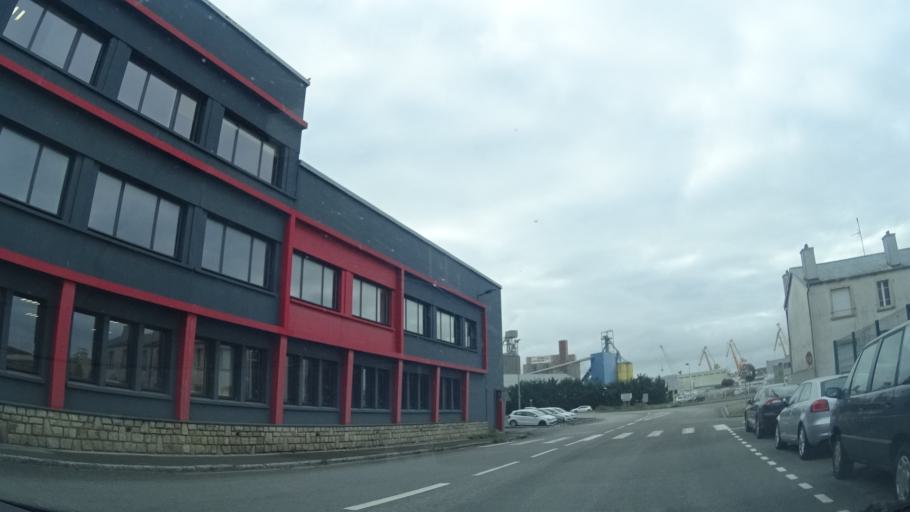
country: FR
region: Brittany
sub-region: Departement du Finistere
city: Brest
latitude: 48.3855
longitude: -4.4748
